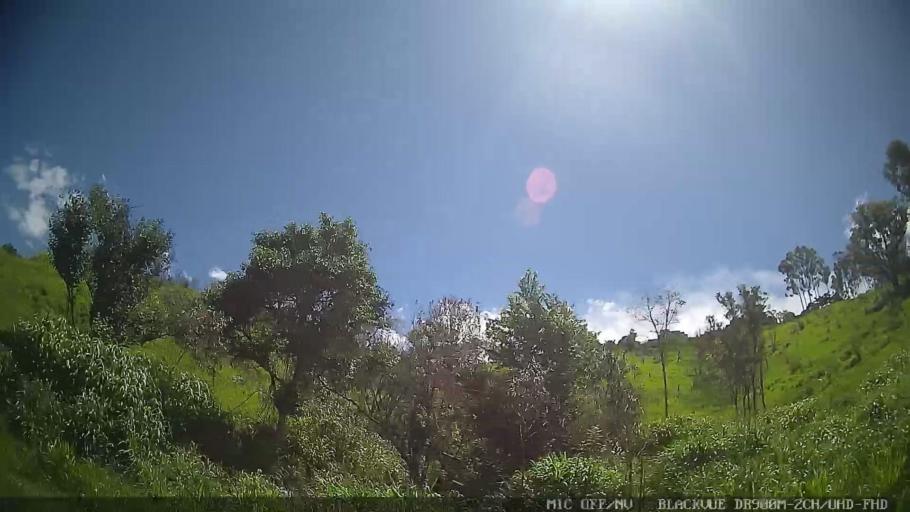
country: BR
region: Sao Paulo
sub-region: Pedreira
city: Pedreira
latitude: -22.7492
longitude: -46.9196
